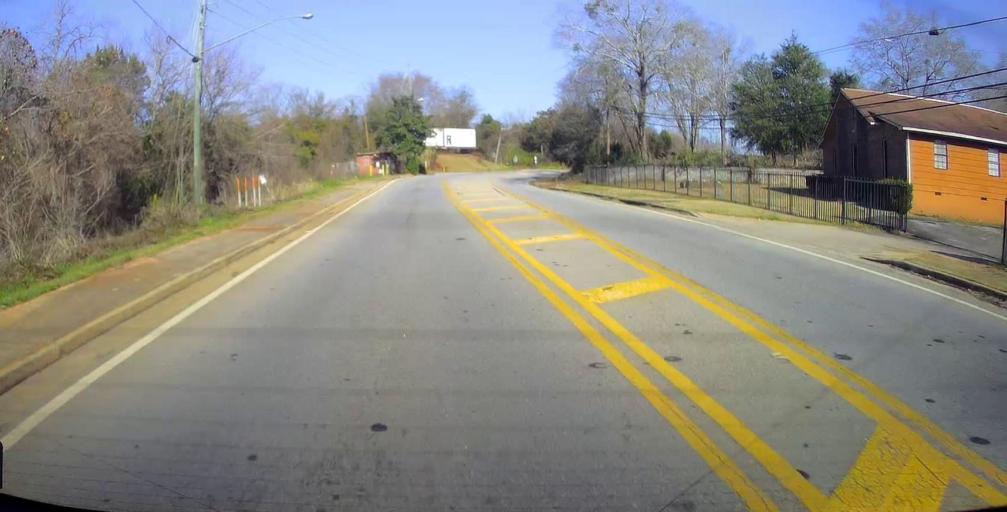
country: US
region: Georgia
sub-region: Macon County
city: Montezuma
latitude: 32.3014
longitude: -84.0350
